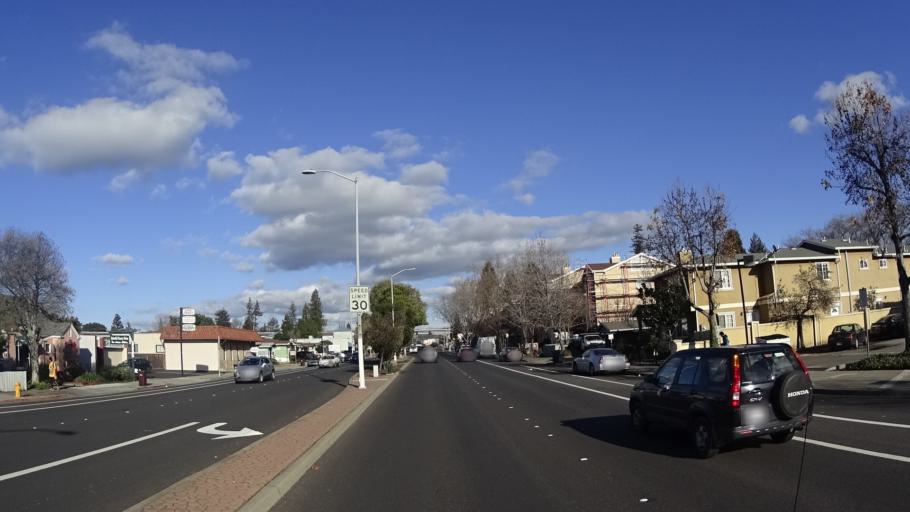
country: US
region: California
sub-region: Alameda County
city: Hayward
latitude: 37.6702
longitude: -122.0916
